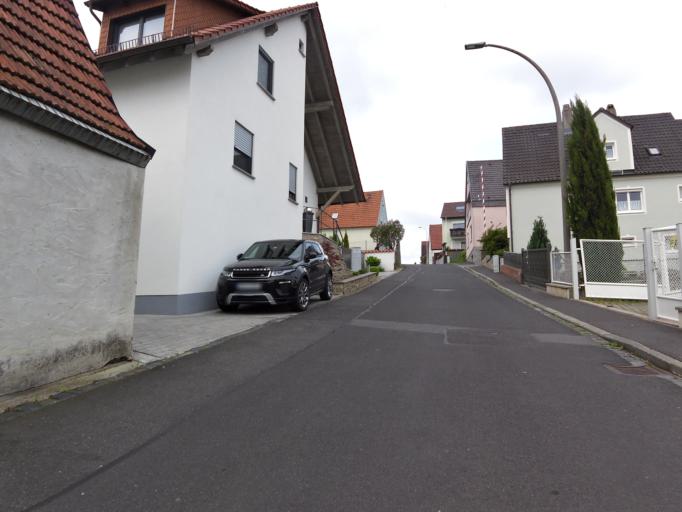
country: DE
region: Bavaria
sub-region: Regierungsbezirk Unterfranken
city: Waldbrunn
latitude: 49.7594
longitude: 9.8014
